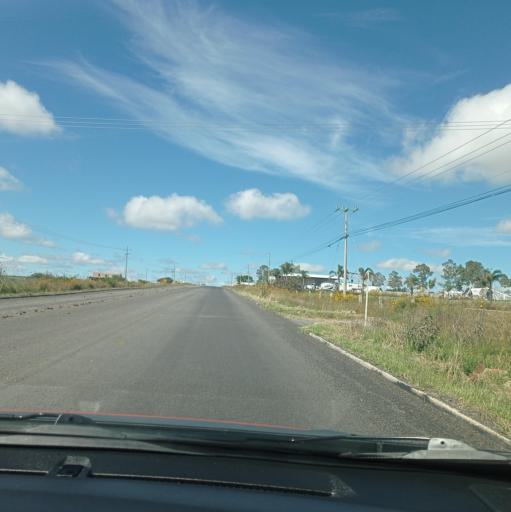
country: MX
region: Jalisco
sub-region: San Julian
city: Colonia Veintitres de Mayo
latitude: 21.0103
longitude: -102.2343
